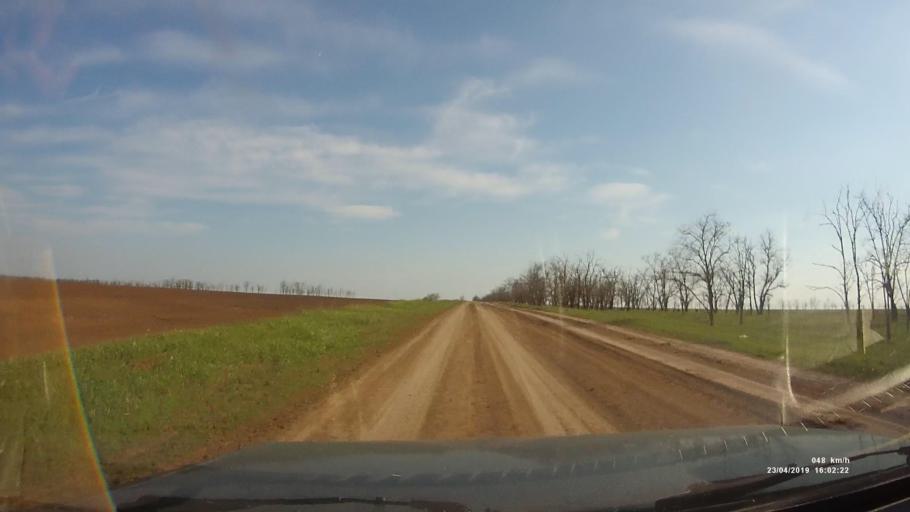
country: RU
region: Rostov
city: Remontnoye
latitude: 46.4948
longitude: 43.1070
